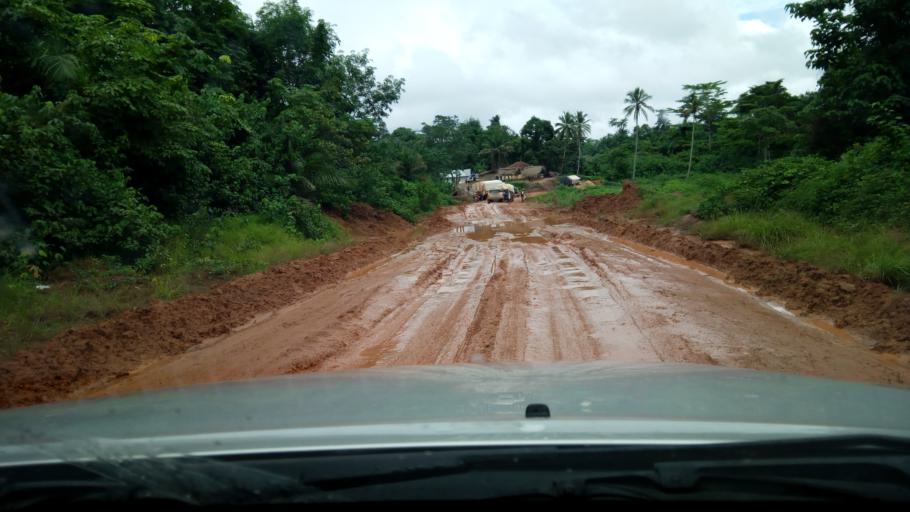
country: CI
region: Dix-Huit Montagnes
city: Toulepleu Guere
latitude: 6.8271
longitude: -8.8116
